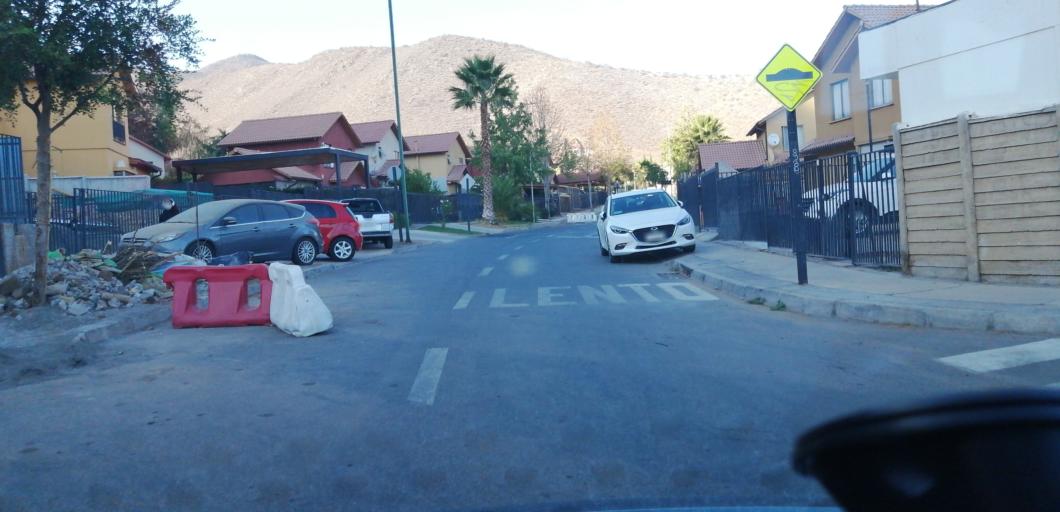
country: CL
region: Santiago Metropolitan
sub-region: Provincia de Santiago
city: Lo Prado
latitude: -33.4539
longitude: -70.8448
